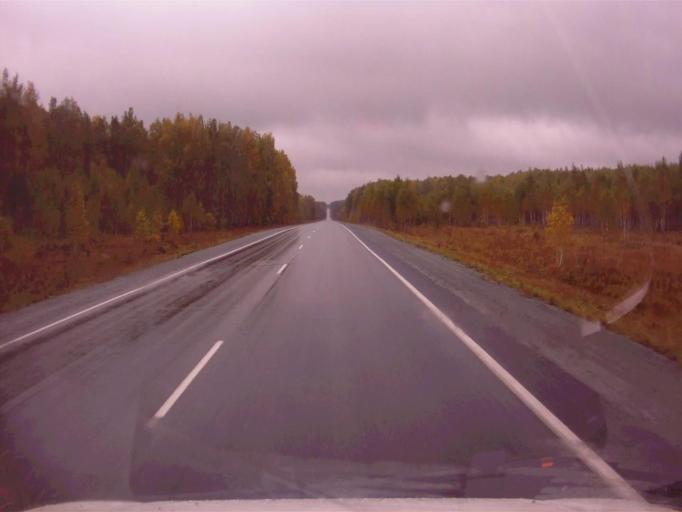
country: RU
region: Chelyabinsk
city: Tayginka
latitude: 55.5092
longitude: 60.6378
